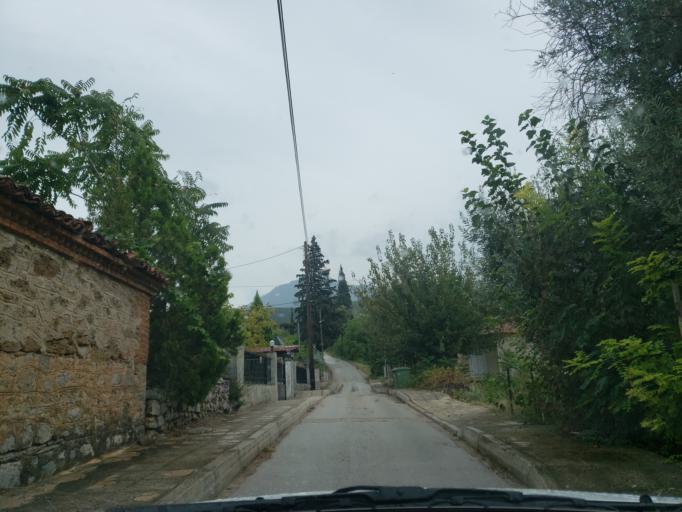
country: GR
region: Central Greece
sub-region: Nomos Fthiotidos
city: Anthili
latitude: 38.7983
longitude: 22.4784
